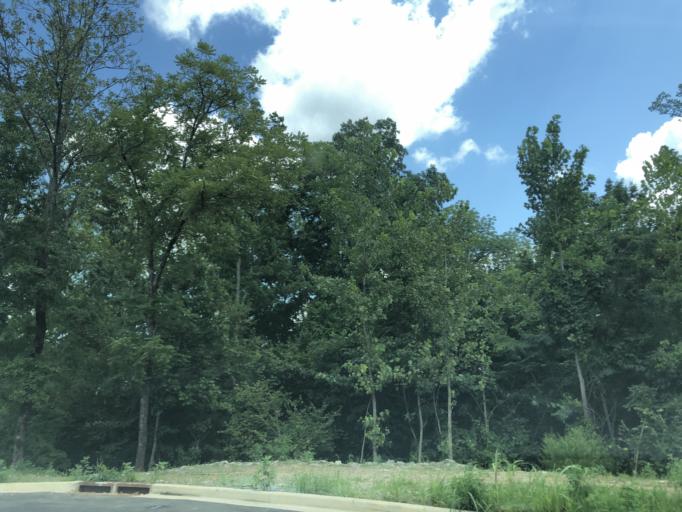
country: US
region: Tennessee
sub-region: Wilson County
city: Green Hill
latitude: 36.2099
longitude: -86.5838
